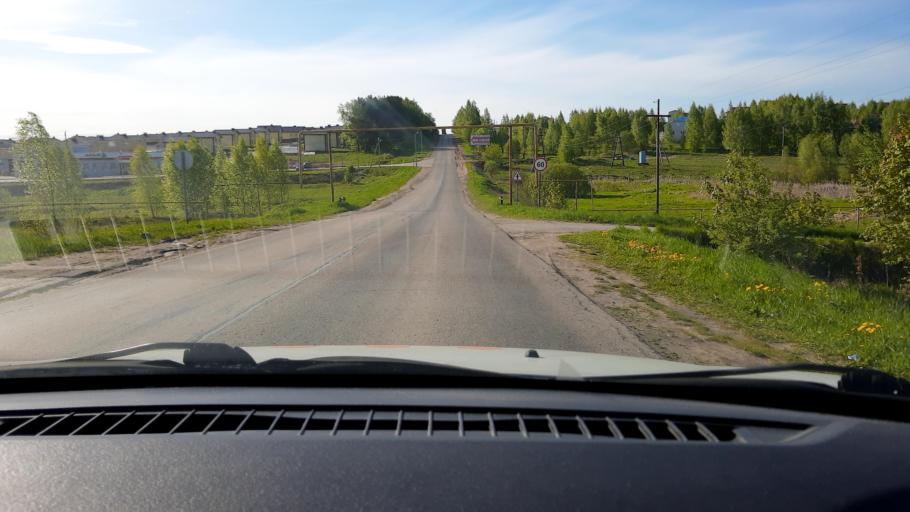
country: RU
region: Nizjnij Novgorod
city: Burevestnik
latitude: 56.1688
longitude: 43.7658
